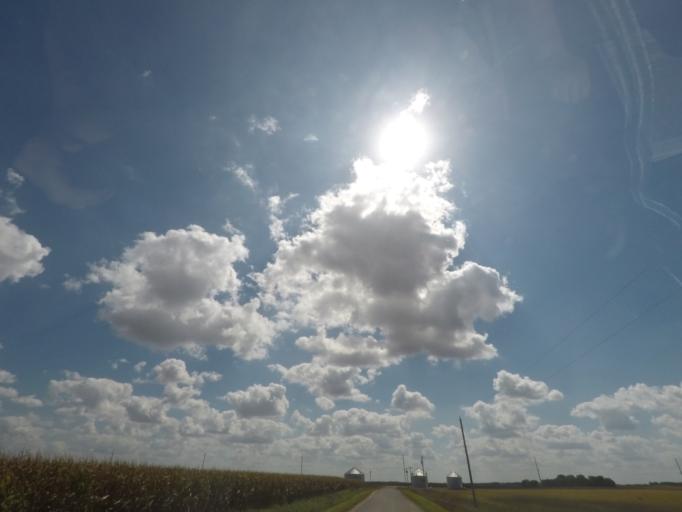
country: US
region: Iowa
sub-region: Story County
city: Nevada
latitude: 42.0365
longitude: -93.3621
